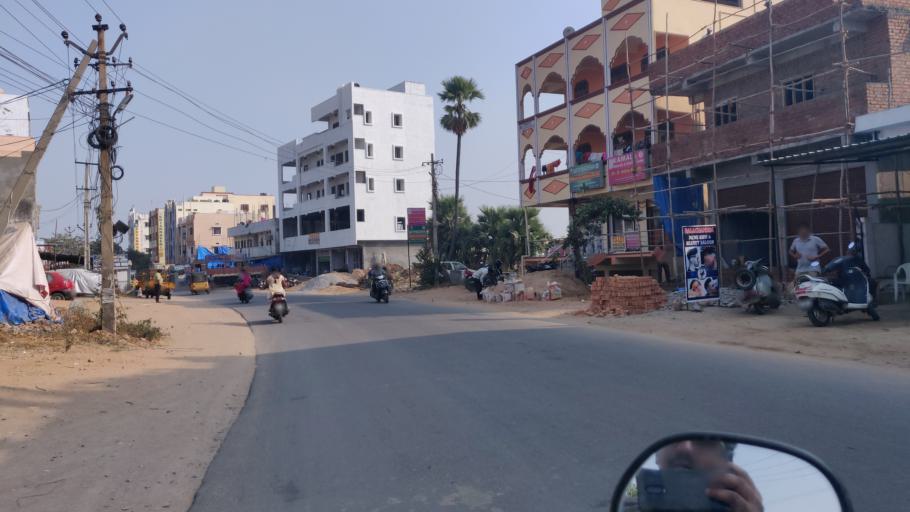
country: IN
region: Telangana
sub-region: Rangareddi
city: Uppal Kalan
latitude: 17.3922
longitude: 78.5974
